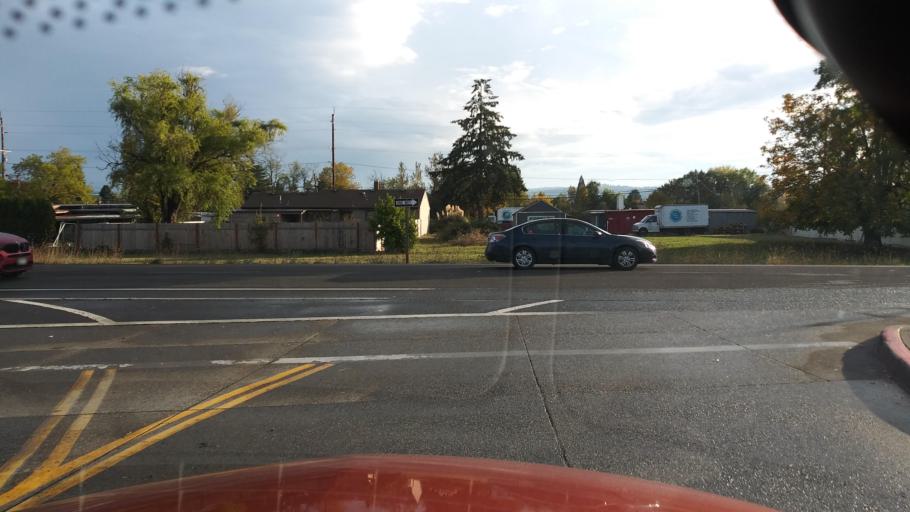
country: US
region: Oregon
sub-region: Washington County
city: Cornelius
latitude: 45.5212
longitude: -123.0686
